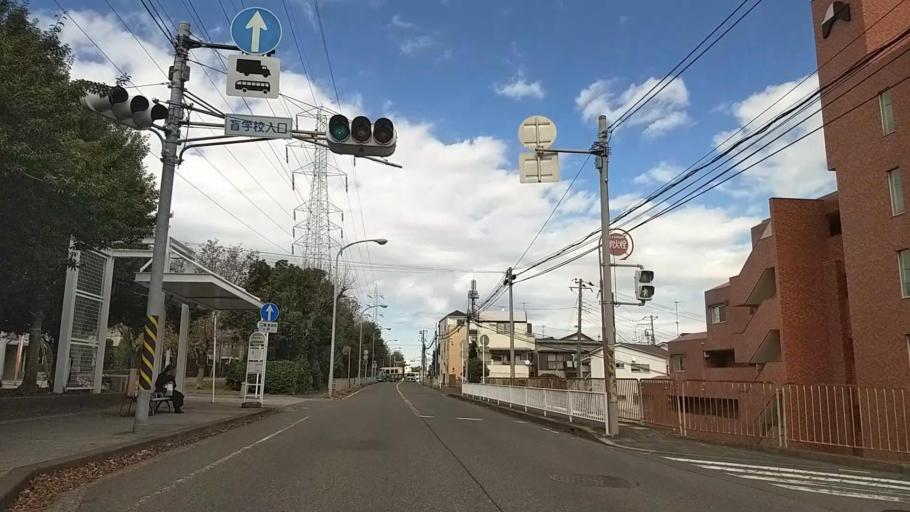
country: JP
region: Kanagawa
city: Yokohama
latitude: 35.4968
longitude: 139.6368
